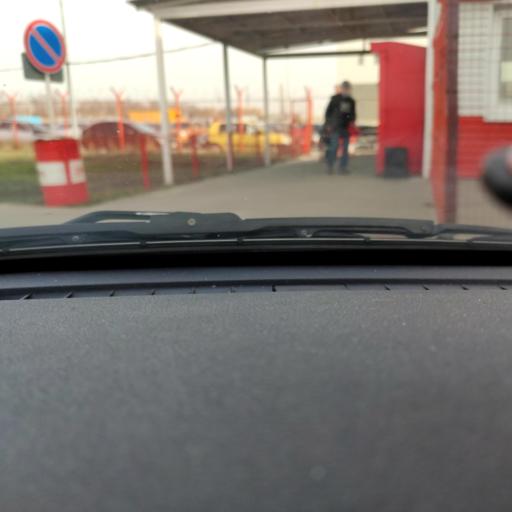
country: RU
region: Voronezj
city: Novaya Usman'
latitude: 51.6208
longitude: 39.3384
